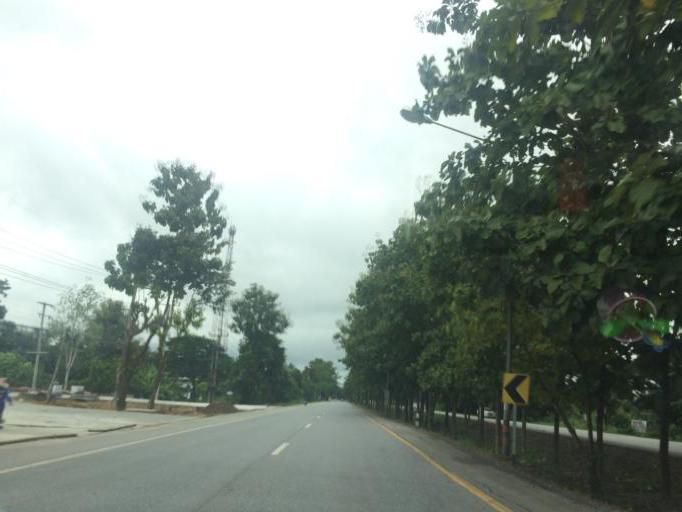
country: TH
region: Chiang Rai
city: Mae Lao
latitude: 19.8017
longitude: 99.7537
